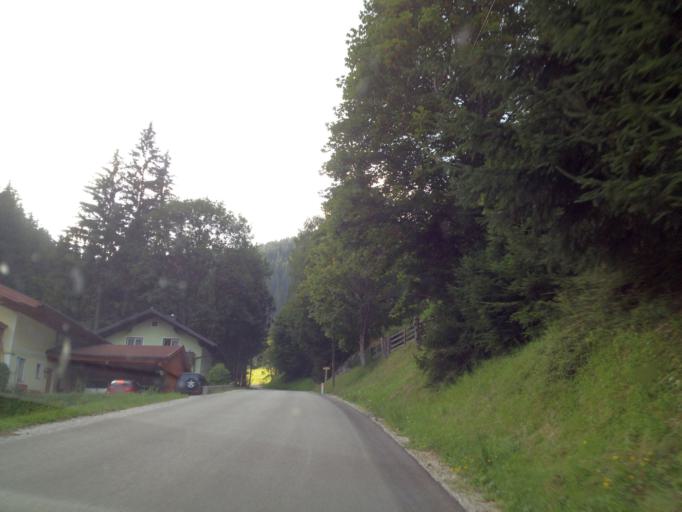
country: AT
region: Styria
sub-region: Politischer Bezirk Liezen
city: Schladming
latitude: 47.3950
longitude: 13.6142
